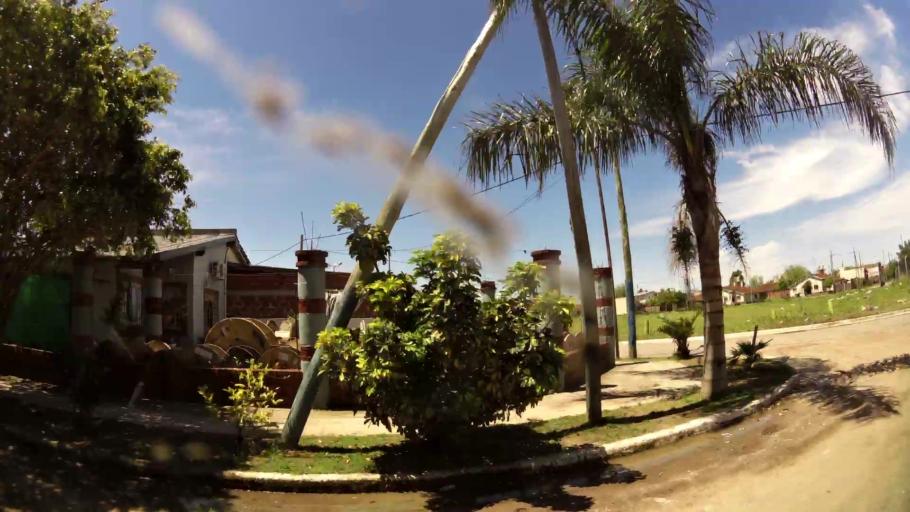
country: AR
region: Buenos Aires
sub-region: Partido de Quilmes
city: Quilmes
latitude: -34.7453
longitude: -58.3107
